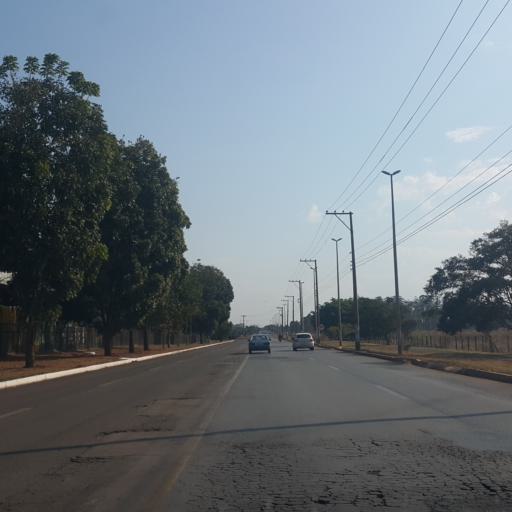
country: BR
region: Federal District
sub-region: Brasilia
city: Brasilia
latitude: -15.8706
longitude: -48.0407
